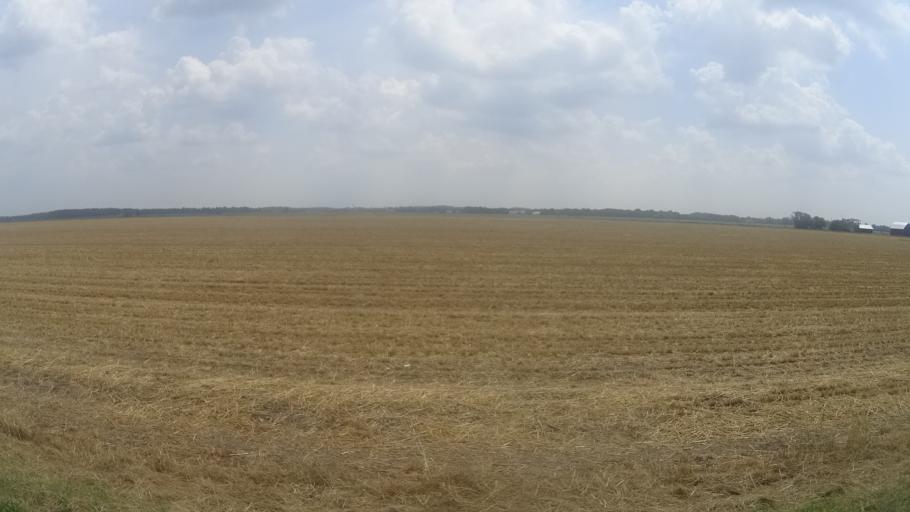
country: US
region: Ohio
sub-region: Huron County
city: Monroeville
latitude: 41.2901
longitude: -82.6921
